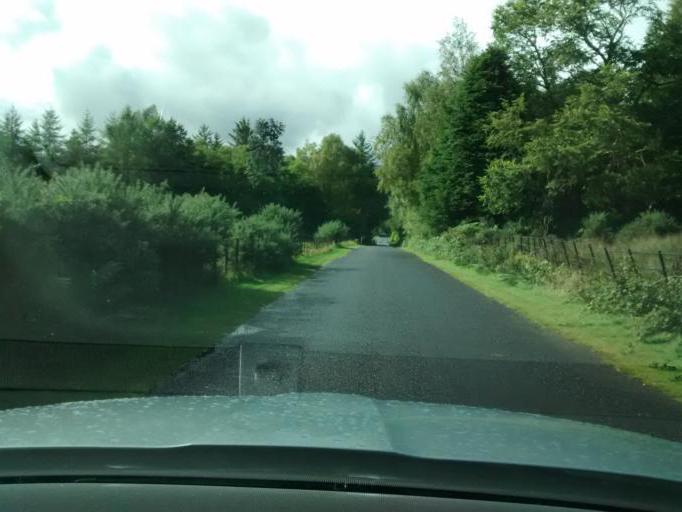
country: GB
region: Scotland
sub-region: North Ayrshire
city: Isle of Arran
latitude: 55.5936
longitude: -5.1592
